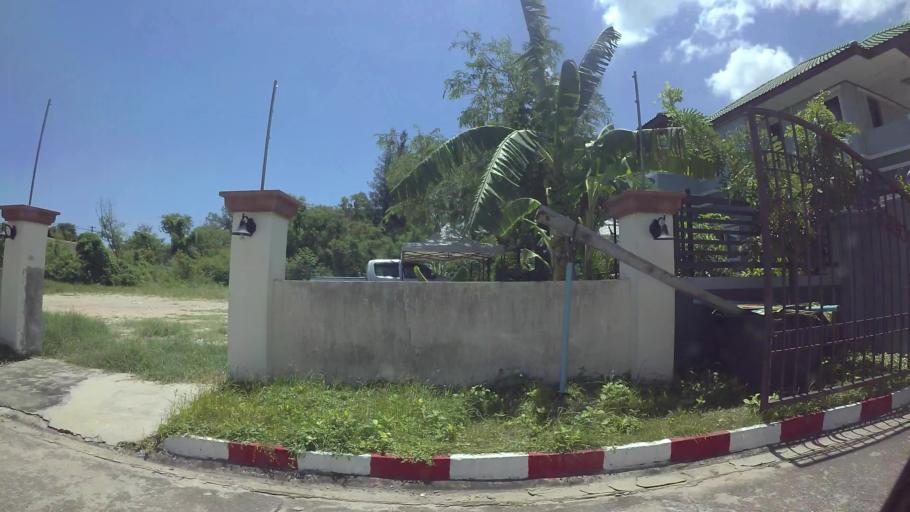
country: TH
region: Chon Buri
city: Si Racha
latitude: 13.1285
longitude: 100.9451
